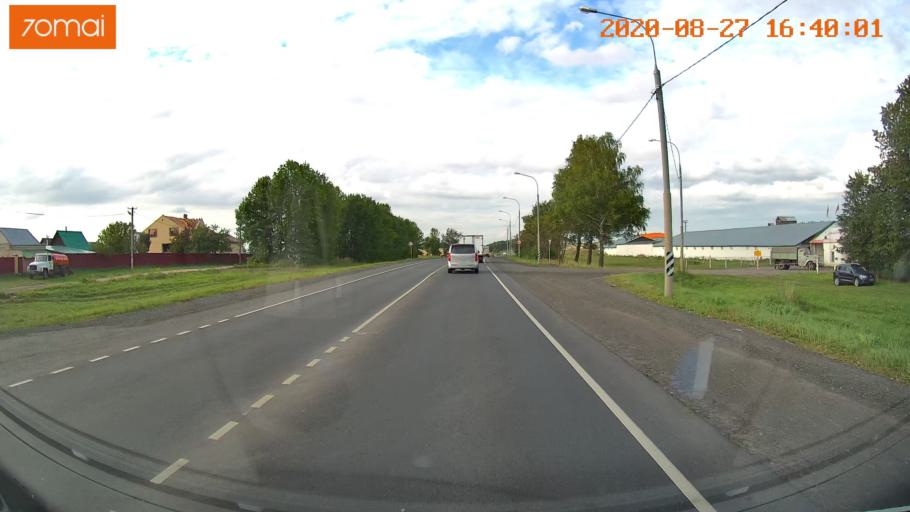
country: RU
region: Vladimir
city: Suzdal'
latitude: 56.3275
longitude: 40.4722
